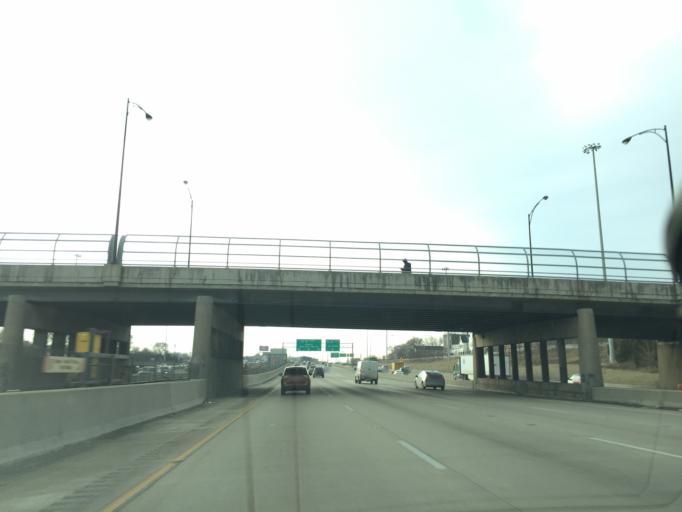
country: US
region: Illinois
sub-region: Cook County
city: Chicago
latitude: 41.8170
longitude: -87.6305
